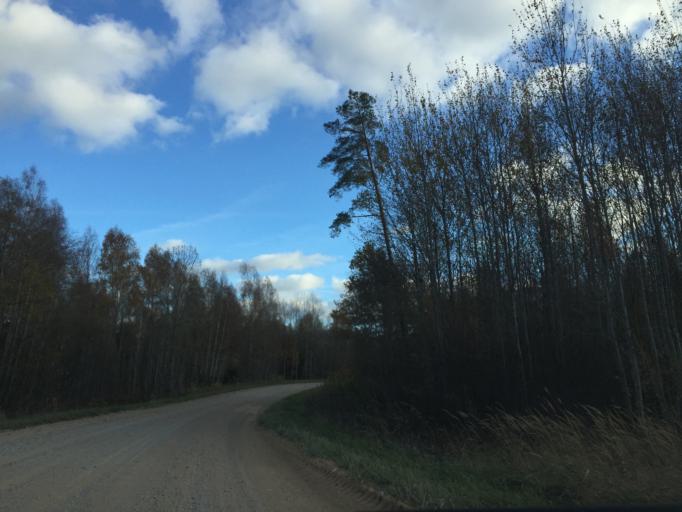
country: LV
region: Tukuma Rajons
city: Tukums
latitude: 56.9622
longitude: 22.9764
